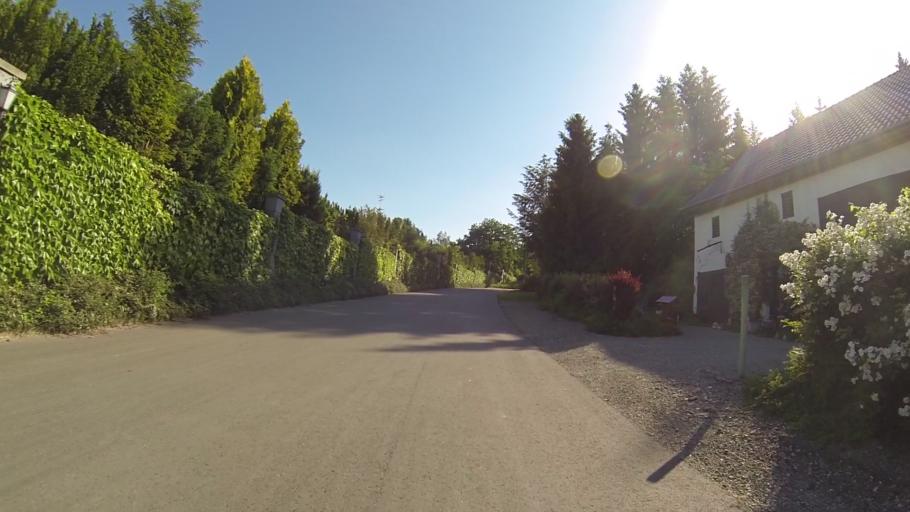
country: DE
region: Baden-Wuerttemberg
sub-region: Tuebingen Region
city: Warthausen
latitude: 48.1630
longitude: 9.7935
